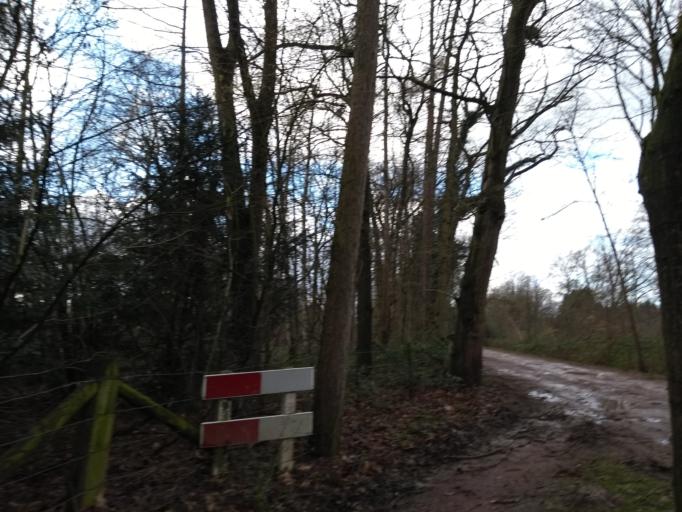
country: NL
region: Overijssel
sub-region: Gemeente Enschede
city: Enschede
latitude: 52.2487
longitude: 6.8783
